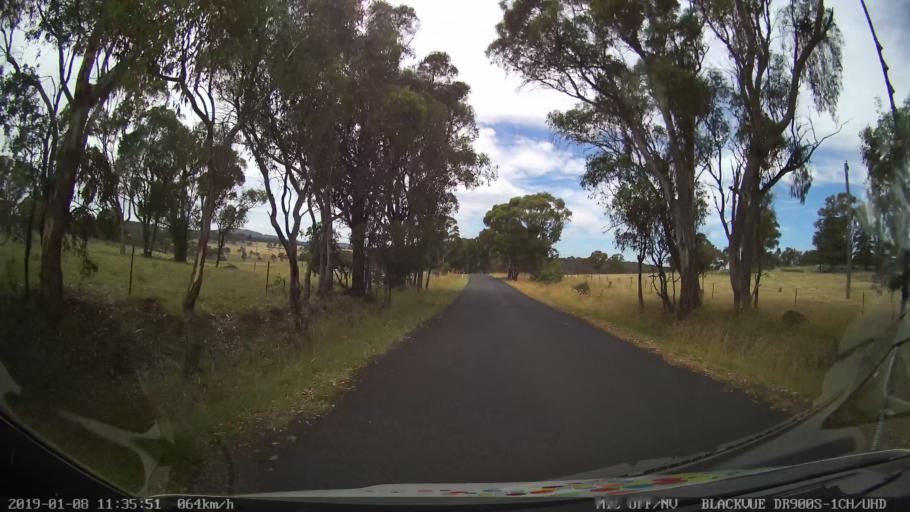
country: AU
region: New South Wales
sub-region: Guyra
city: Guyra
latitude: -30.3411
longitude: 151.5392
